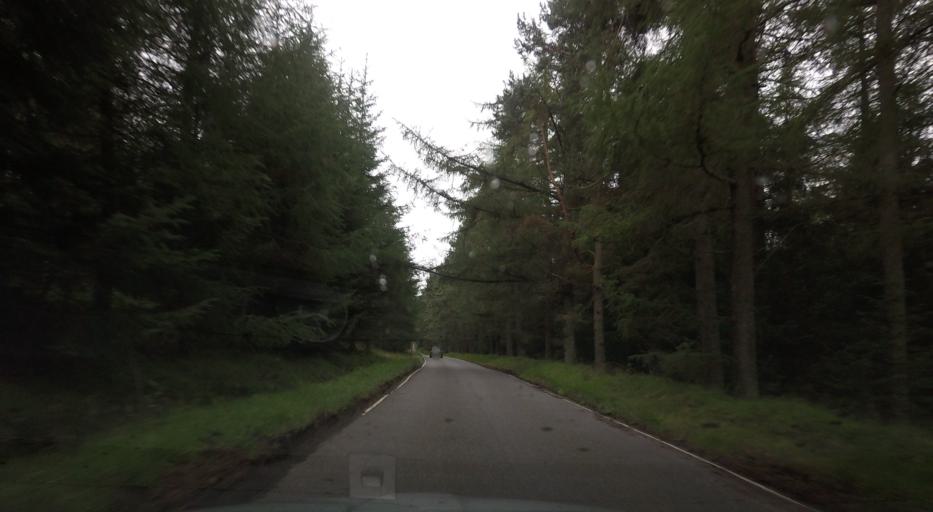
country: GB
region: Scotland
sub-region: Aberdeenshire
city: Banchory
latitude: 56.9498
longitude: -2.5808
